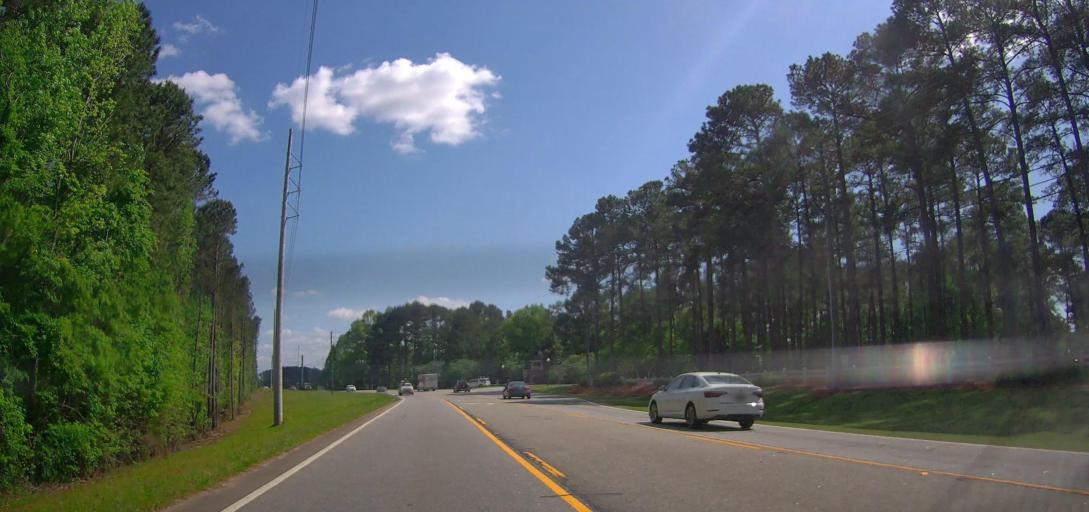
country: US
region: Georgia
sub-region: Putnam County
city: Jefferson
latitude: 33.4714
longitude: -83.2456
